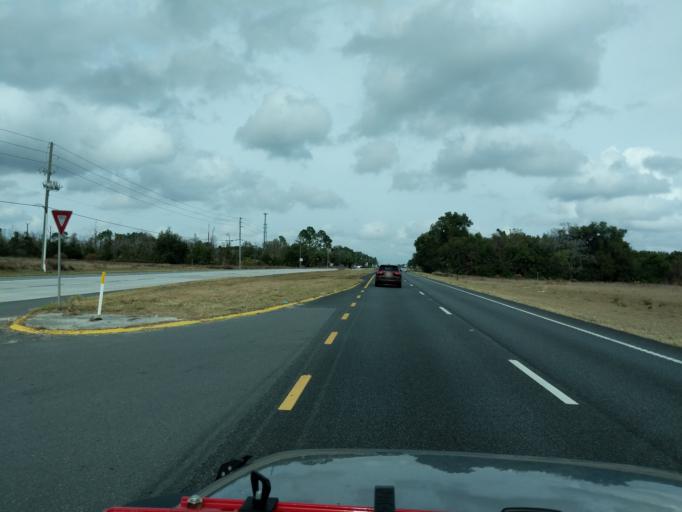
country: US
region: Florida
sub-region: Orange County
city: Tangerine
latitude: 28.7650
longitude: -81.6245
